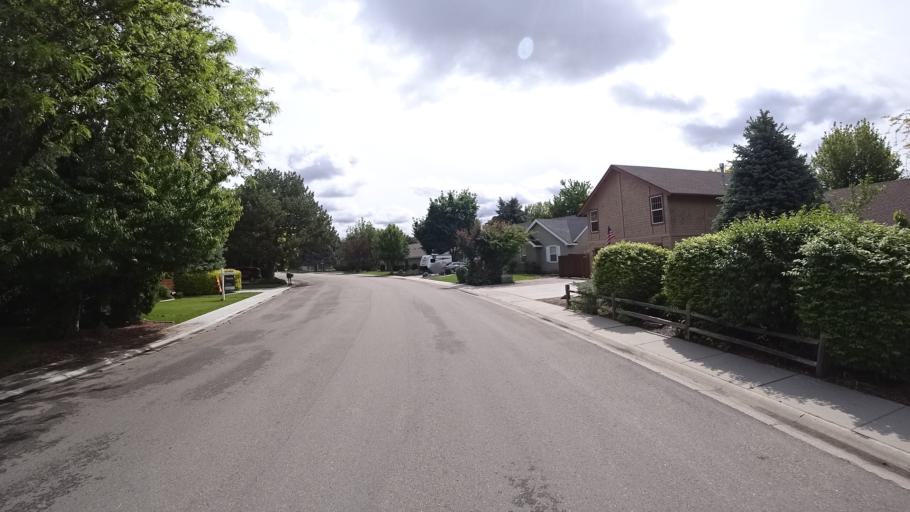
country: US
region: Idaho
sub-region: Ada County
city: Eagle
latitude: 43.7014
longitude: -116.3496
